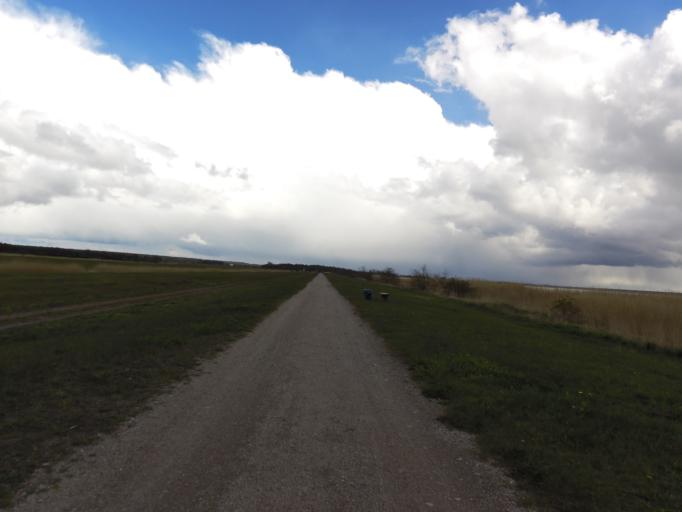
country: DE
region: Mecklenburg-Vorpommern
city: Born
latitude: 54.3822
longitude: 12.4763
